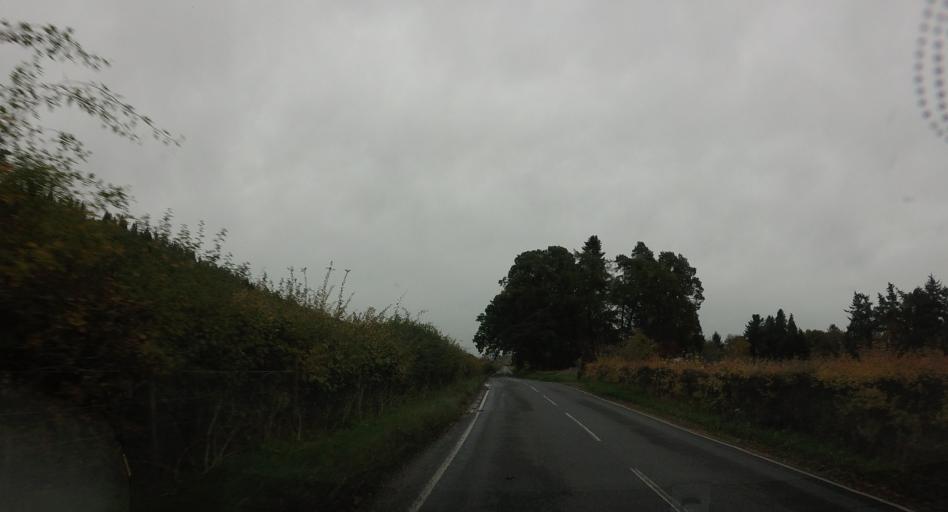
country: GB
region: Scotland
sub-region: Perth and Kinross
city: Bankfoot
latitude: 56.5444
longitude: -3.4956
